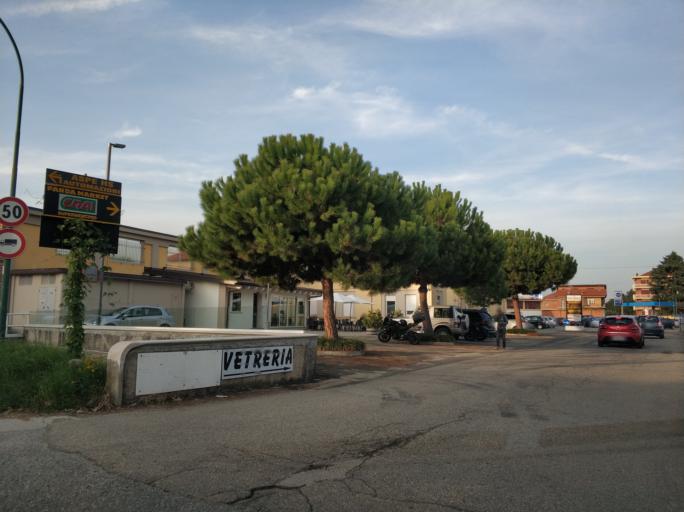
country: IT
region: Piedmont
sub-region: Provincia di Torino
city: Mathi
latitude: 45.2544
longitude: 7.5472
